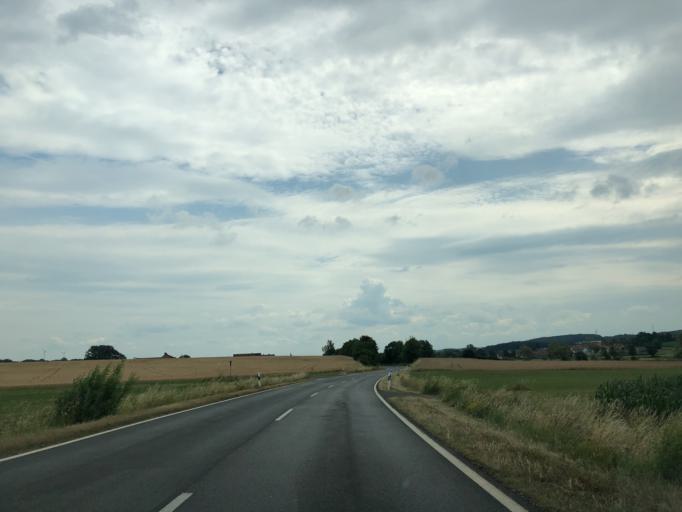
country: DE
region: Bavaria
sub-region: Regierungsbezirk Mittelfranken
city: Wachenroth
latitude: 49.7474
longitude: 10.6784
